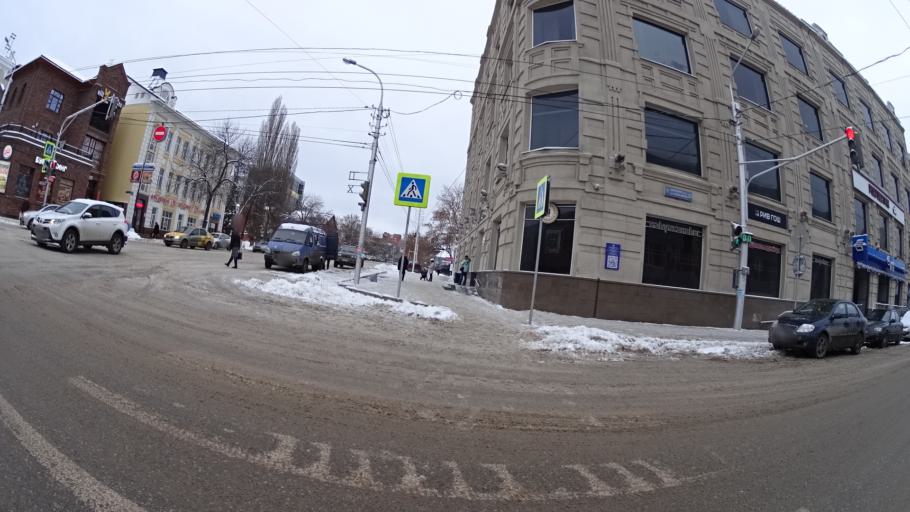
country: RU
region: Bashkortostan
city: Ufa
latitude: 54.7256
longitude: 55.9407
